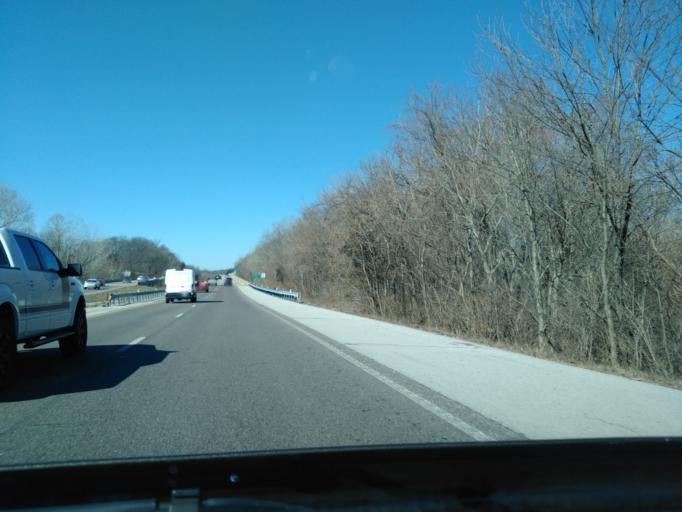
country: US
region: Missouri
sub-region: Saint Louis County
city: Fenton
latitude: 38.5165
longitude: -90.4320
